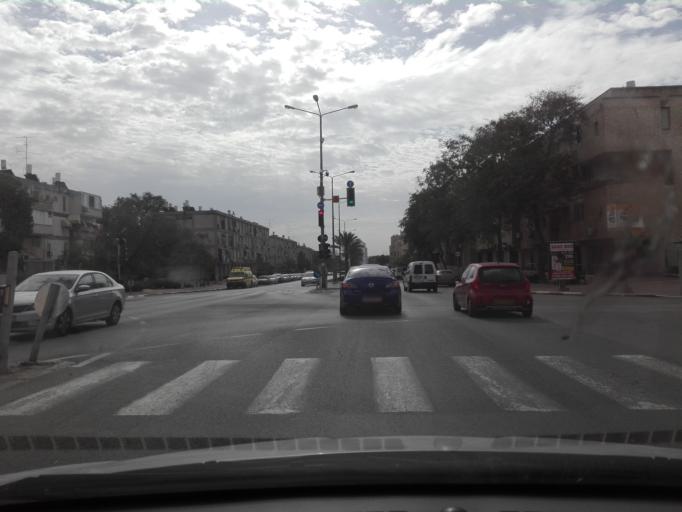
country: IL
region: Southern District
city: Beersheba
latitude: 31.2698
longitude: 34.7980
